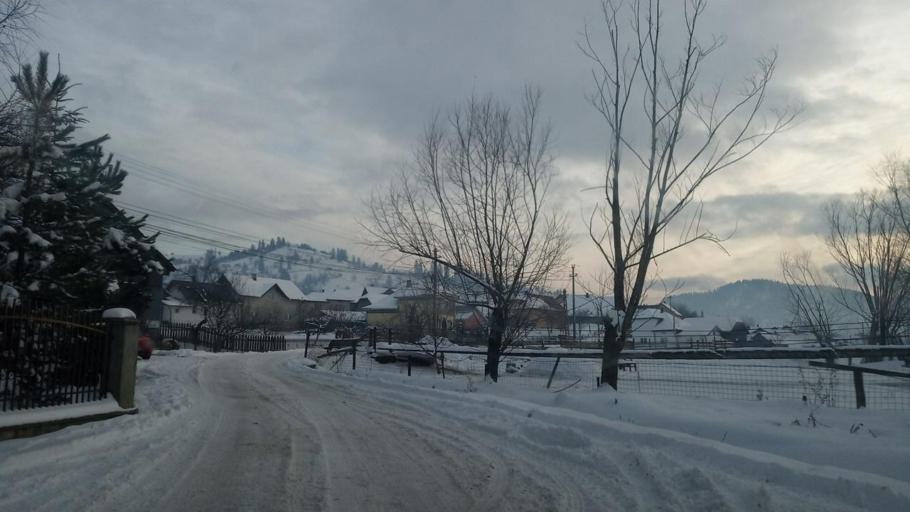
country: RO
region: Suceava
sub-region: Comuna Frasin
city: Plutonita
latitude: 47.5031
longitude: 25.7966
